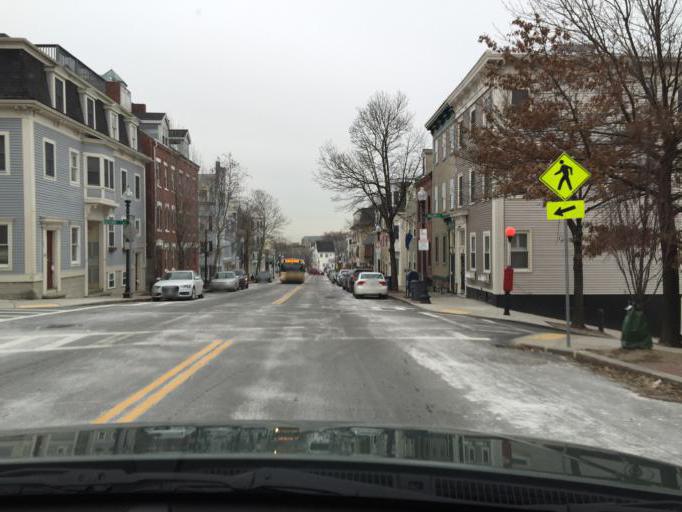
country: US
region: Massachusetts
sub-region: Suffolk County
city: Boston
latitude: 42.3800
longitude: -71.0647
